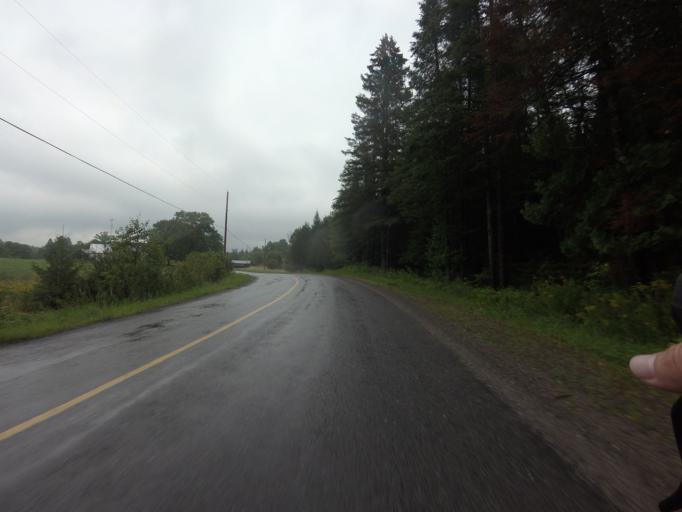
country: CA
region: Ontario
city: Perth
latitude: 45.0583
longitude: -76.5729
